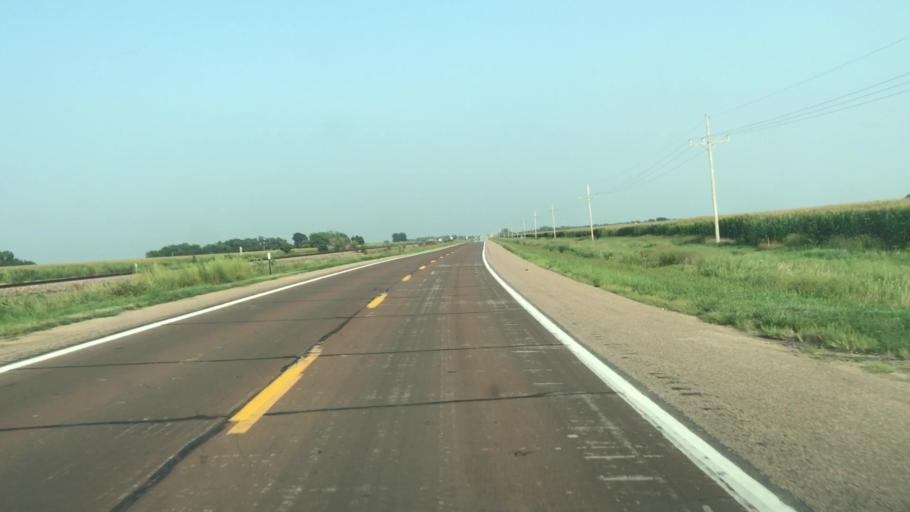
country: US
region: Nebraska
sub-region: Hall County
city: Grand Island
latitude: 40.9670
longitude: -98.4456
